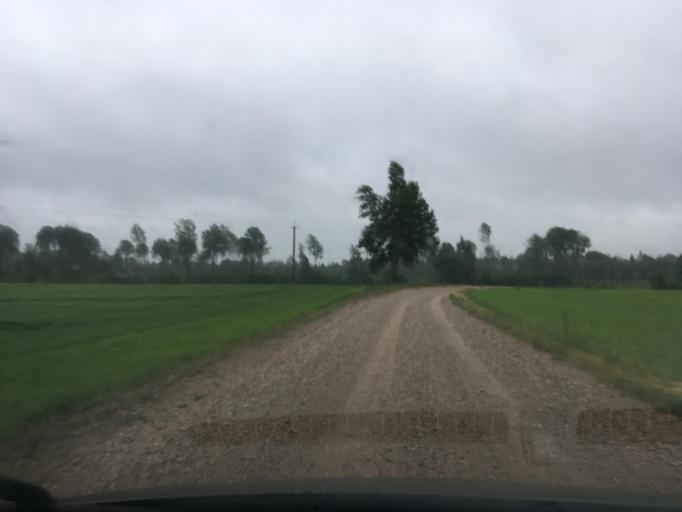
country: EE
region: Laeaene
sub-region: Lihula vald
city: Lihula
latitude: 58.6175
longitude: 23.8253
